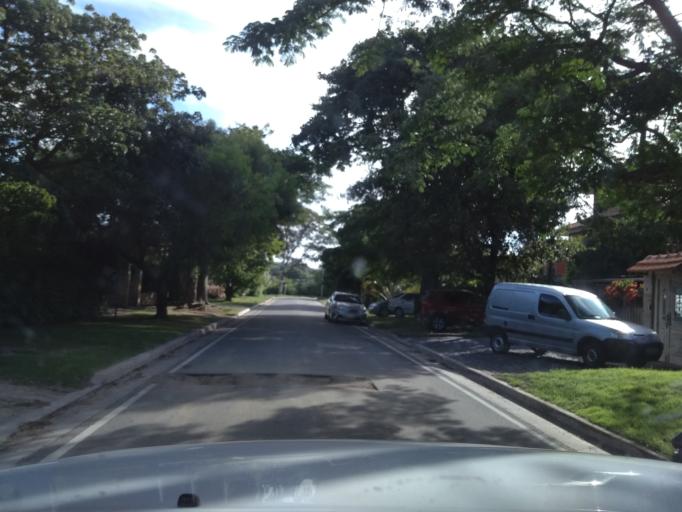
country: UY
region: Canelones
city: Barra de Carrasco
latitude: -34.8707
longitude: -56.0374
